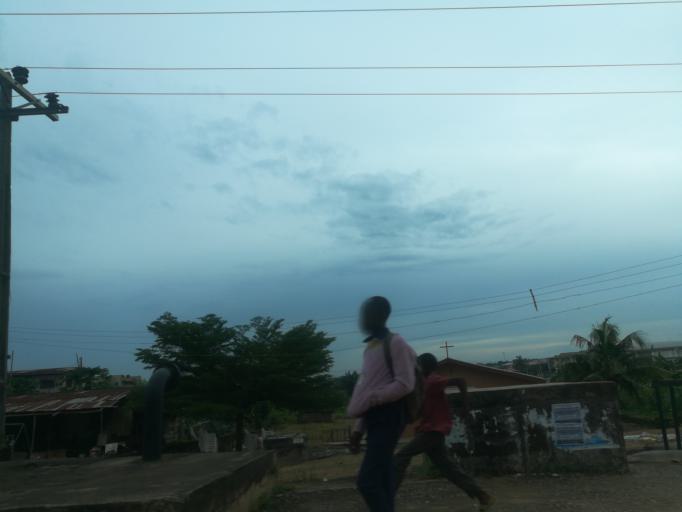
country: NG
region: Oyo
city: Egbeda
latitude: 7.3851
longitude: 3.9920
